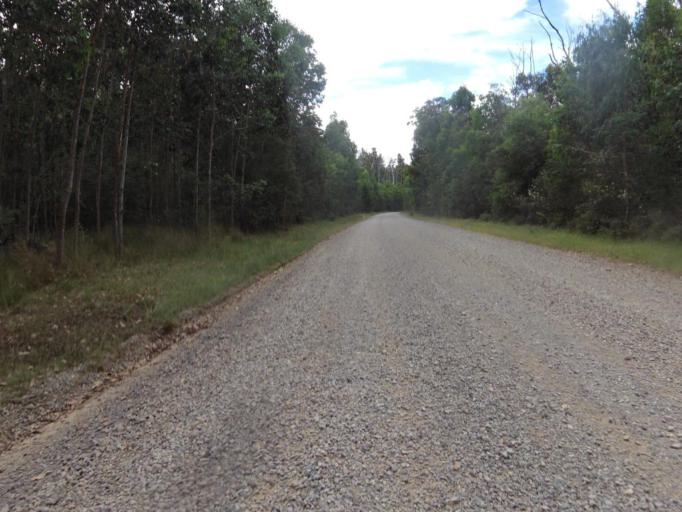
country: AU
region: Victoria
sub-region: Yarra Ranges
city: Healesville
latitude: -37.4006
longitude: 145.5598
